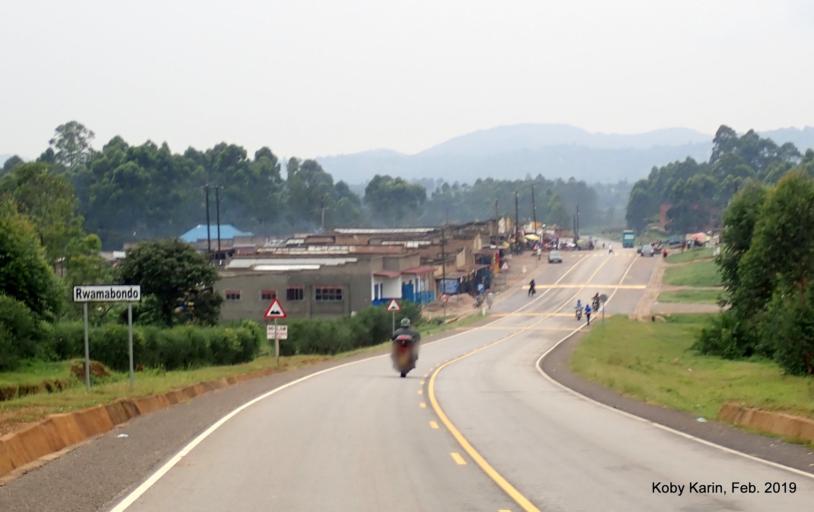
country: UG
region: Western Region
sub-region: Mitoma District
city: Mitoma
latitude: -0.7610
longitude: 30.1630
